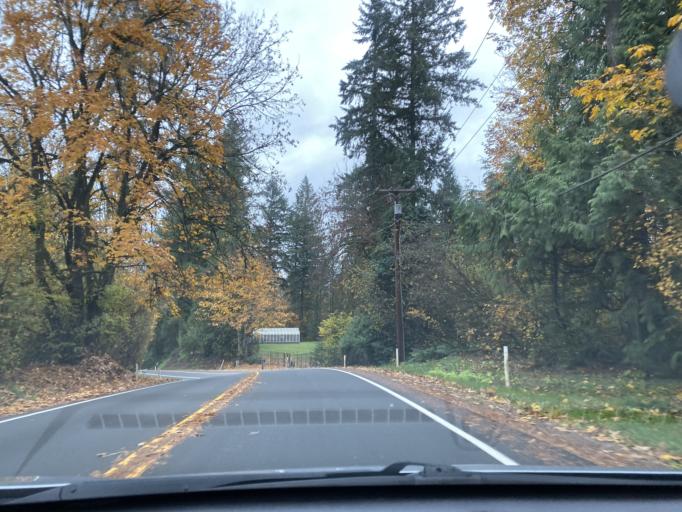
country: US
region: Washington
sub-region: King County
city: Lake Morton-Berrydale
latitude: 47.3003
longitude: -122.0921
